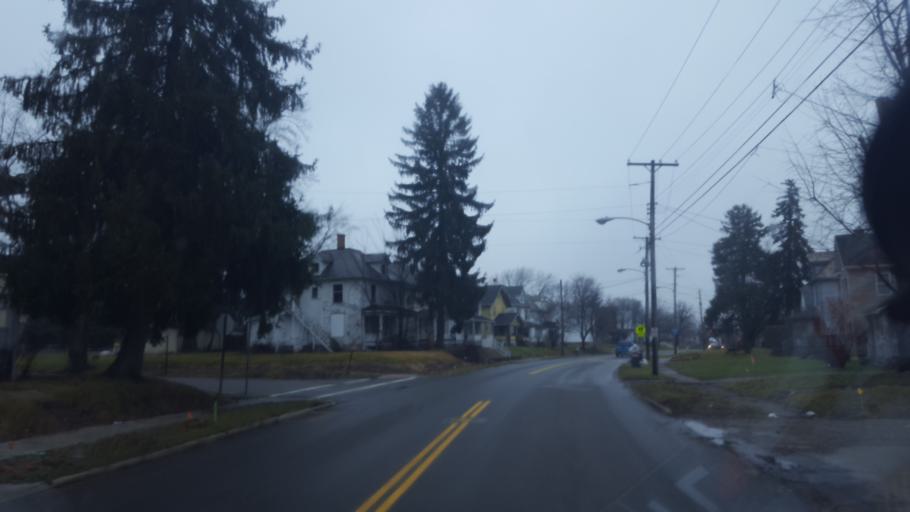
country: US
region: Ohio
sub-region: Richland County
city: Mansfield
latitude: 40.7439
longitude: -82.5164
